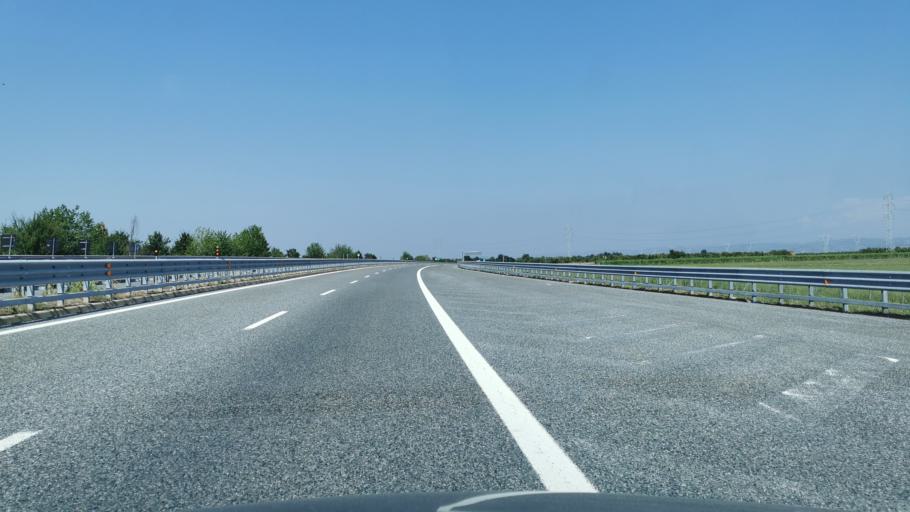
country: IT
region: Piedmont
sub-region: Provincia di Cuneo
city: Magliano Alpi
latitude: 44.4799
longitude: 7.7954
